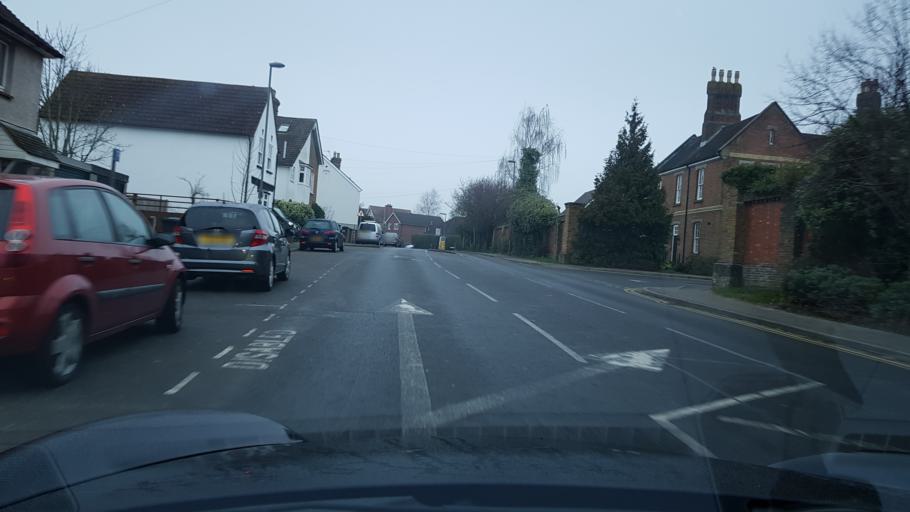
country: GB
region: England
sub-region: Surrey
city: Guildford
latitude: 51.2552
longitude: -0.5909
